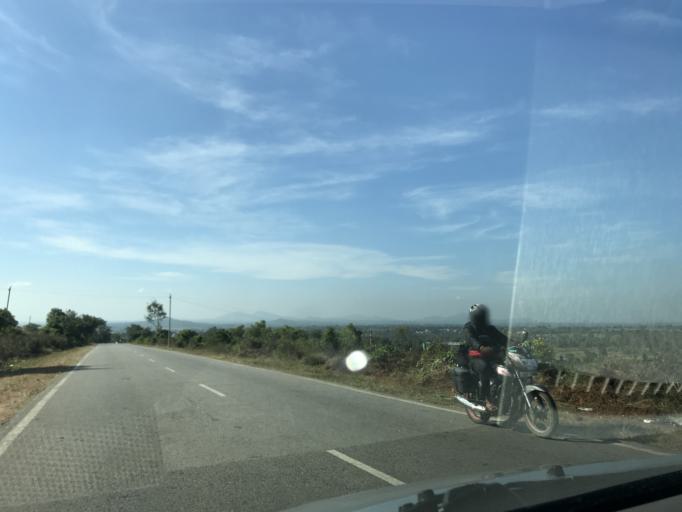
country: IN
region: Karnataka
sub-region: Mysore
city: Nanjangud
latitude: 12.1385
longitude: 76.5091
